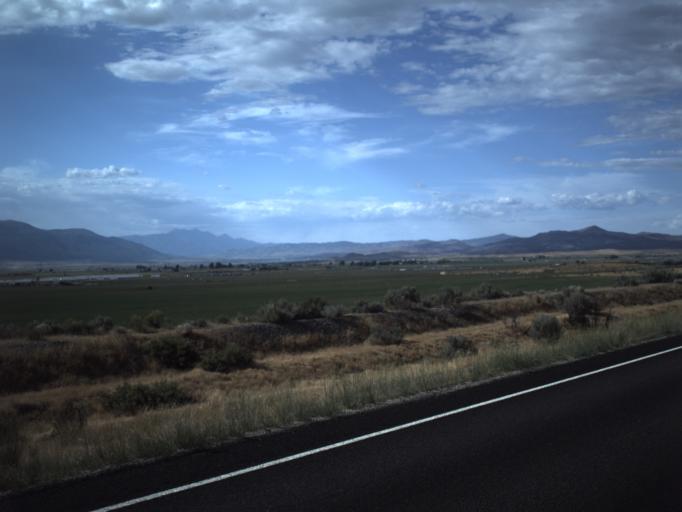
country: US
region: Utah
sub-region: Sanpete County
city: Ephraim
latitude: 39.4334
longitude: -111.5529
